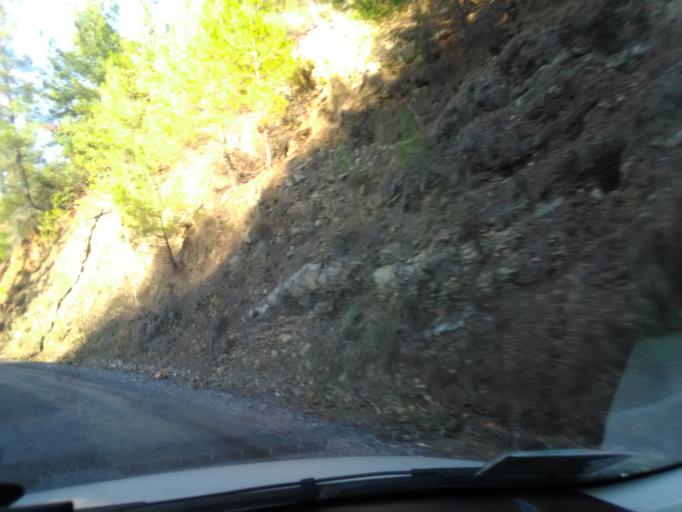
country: TR
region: Antalya
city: Gazipasa
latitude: 36.3111
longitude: 32.4131
